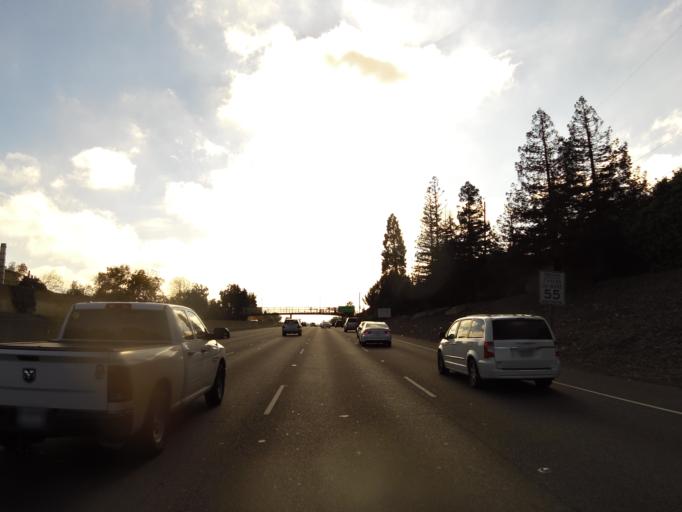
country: US
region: California
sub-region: Sacramento County
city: Sacramento
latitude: 38.5472
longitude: -121.4741
